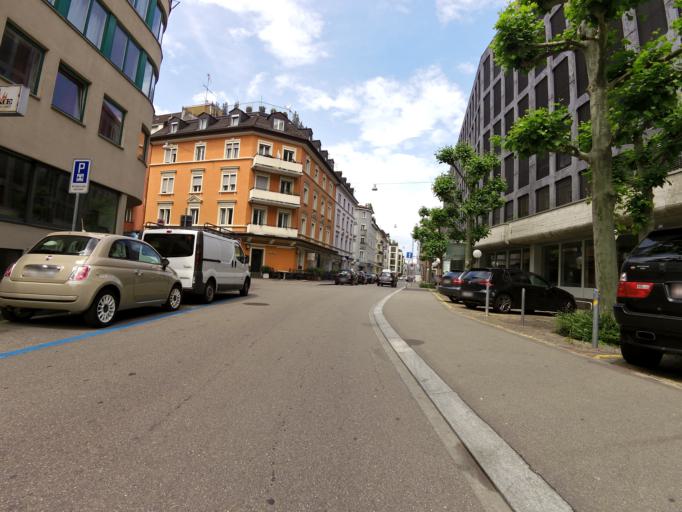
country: CH
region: Zurich
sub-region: Bezirk Zuerich
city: Zuerich (Kreis 4) / Langstrasse
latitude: 47.3743
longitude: 8.5311
